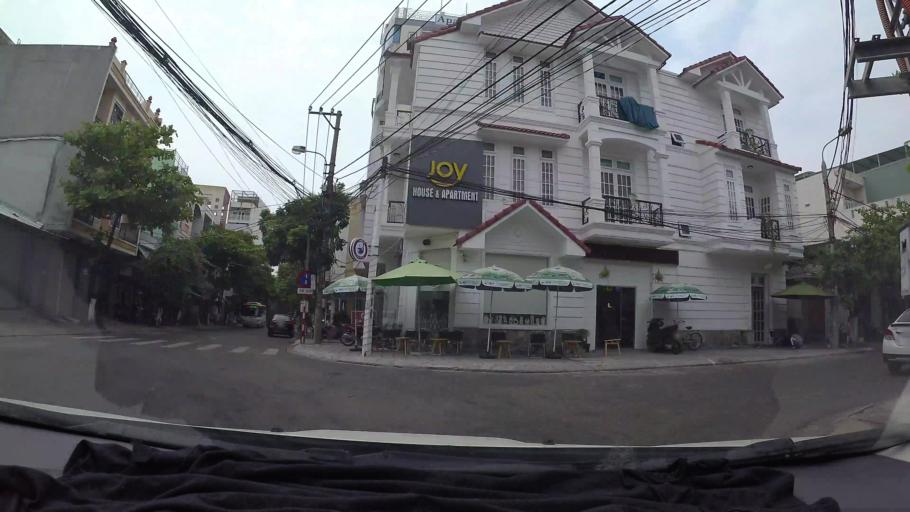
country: VN
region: Da Nang
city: Da Nang
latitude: 16.0865
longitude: 108.2199
